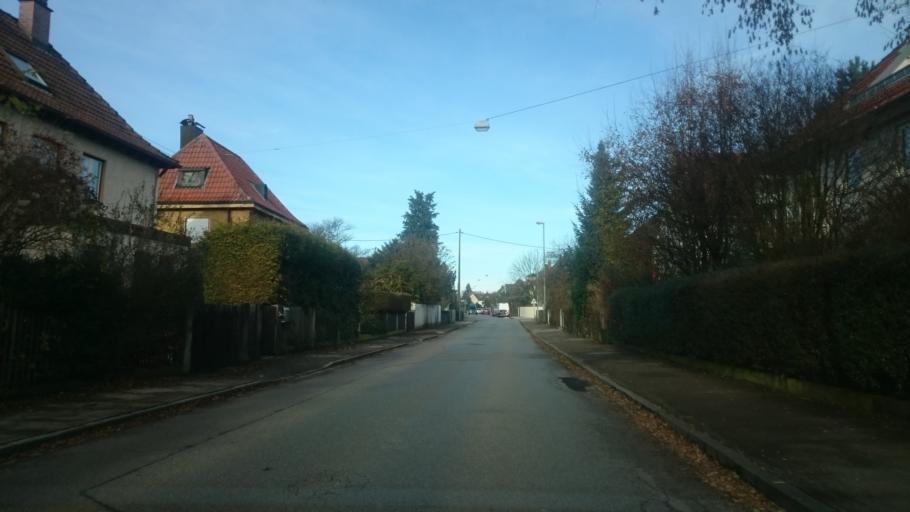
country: DE
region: Bavaria
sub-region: Swabia
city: Friedberg
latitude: 48.3475
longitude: 10.9407
